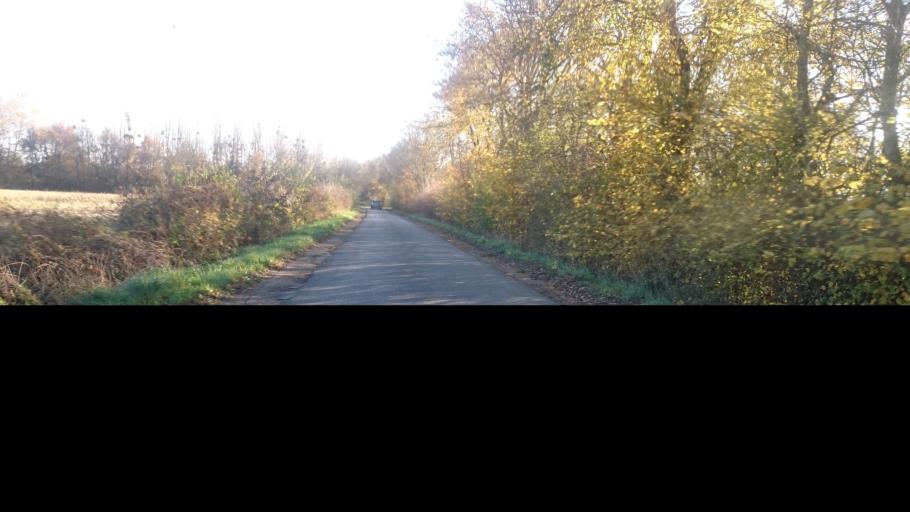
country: FR
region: Bourgogne
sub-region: Departement de Saone-et-Loire
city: Tournus
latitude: 46.5682
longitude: 4.9175
